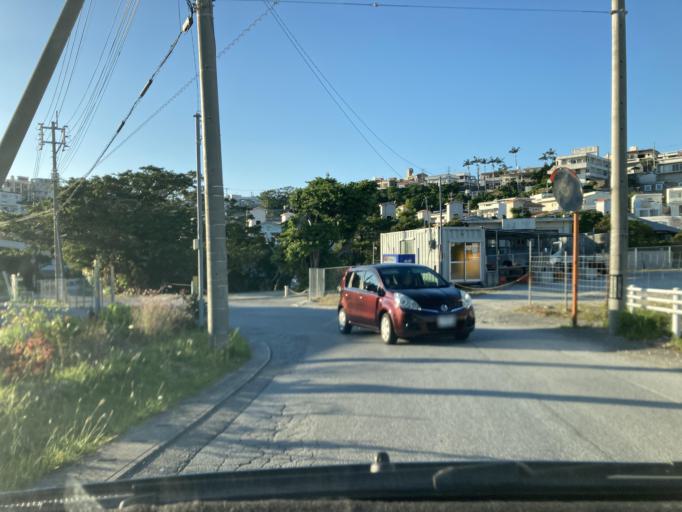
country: JP
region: Okinawa
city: Naha-shi
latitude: 26.2140
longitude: 127.7279
